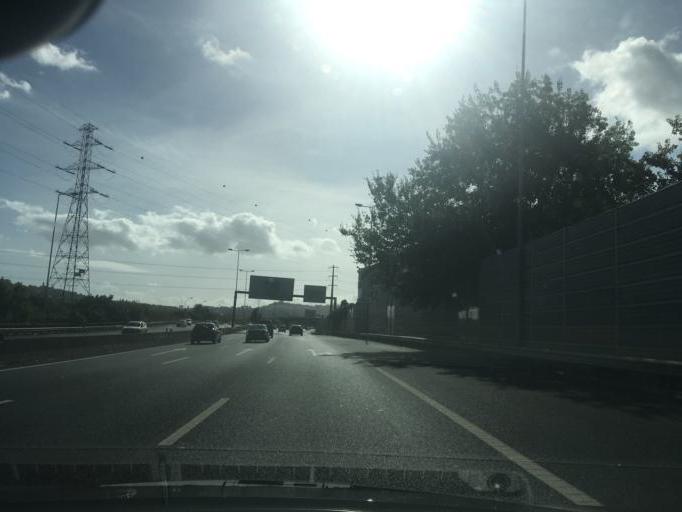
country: PT
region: Lisbon
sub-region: Odivelas
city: Odivelas
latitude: 38.7824
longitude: -9.1855
